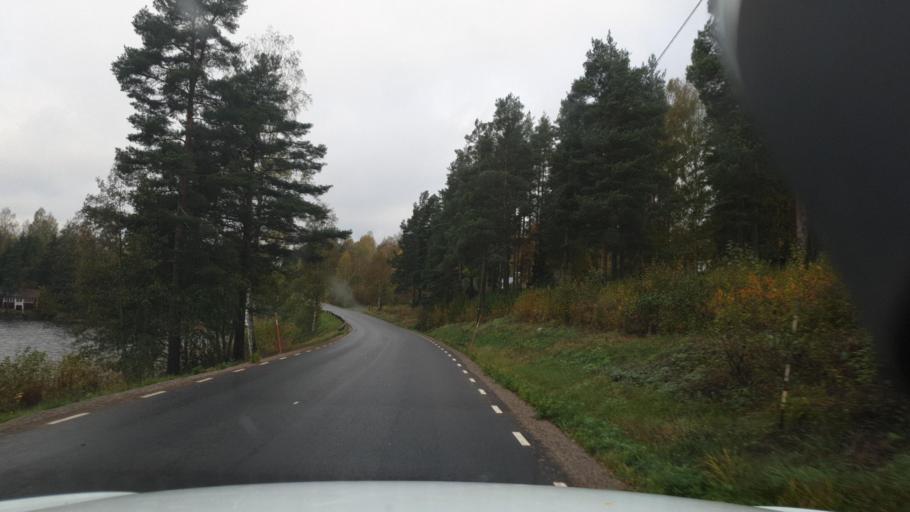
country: SE
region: Vaermland
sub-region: Arvika Kommun
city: Arvika
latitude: 59.6646
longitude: 12.6839
